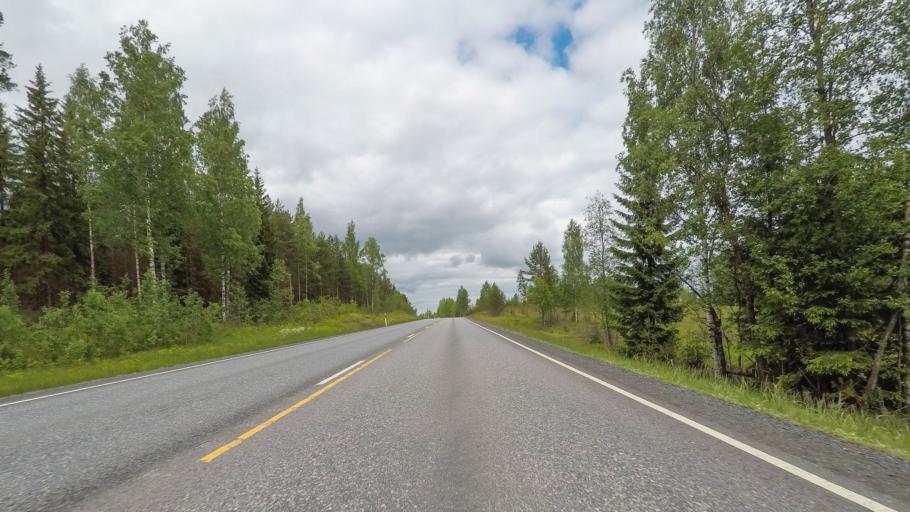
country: FI
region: Central Finland
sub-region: Joutsa
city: Joutsa
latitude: 61.6842
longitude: 26.0556
